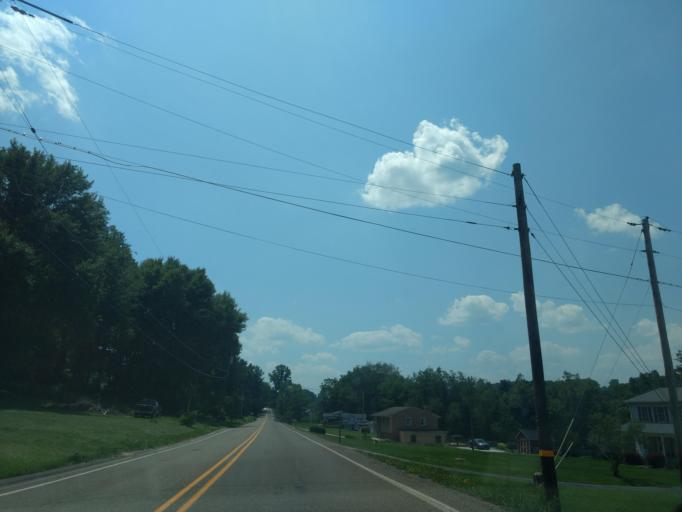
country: US
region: Pennsylvania
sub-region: Butler County
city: Zelienople
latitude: 40.8229
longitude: -80.0995
